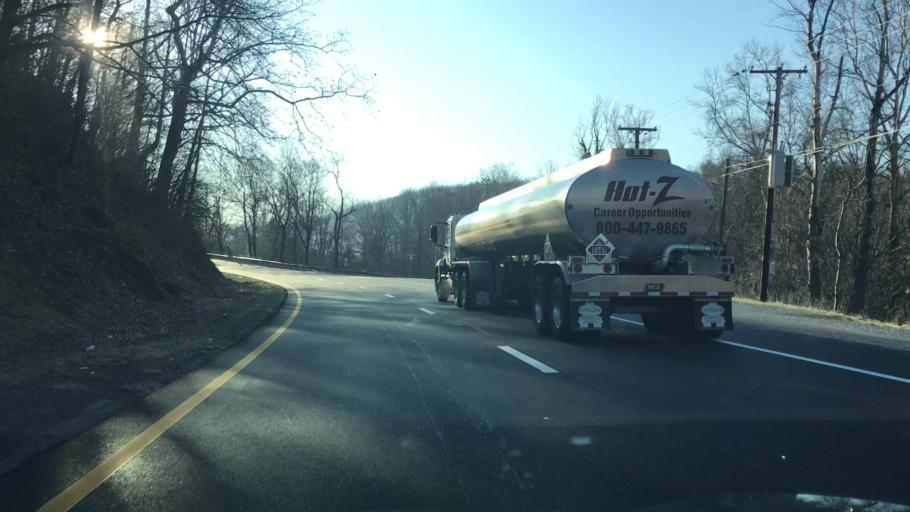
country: US
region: Virginia
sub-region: Botetourt County
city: Blue Ridge
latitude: 37.3888
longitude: -79.7411
